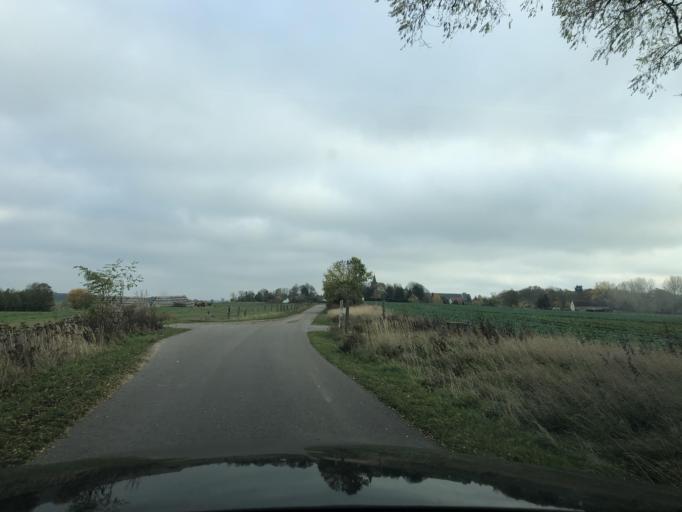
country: DE
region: Mecklenburg-Vorpommern
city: Kessin
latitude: 53.7476
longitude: 13.3405
